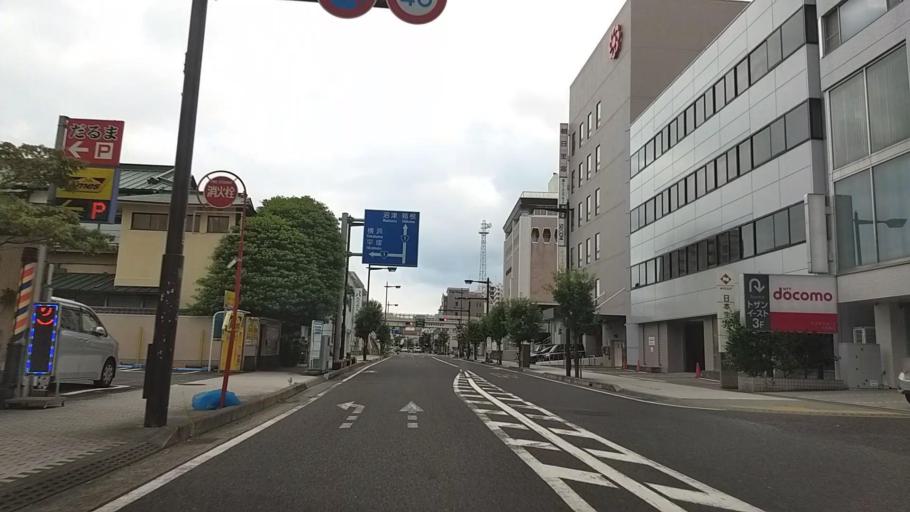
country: JP
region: Kanagawa
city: Odawara
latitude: 35.2517
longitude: 139.1593
